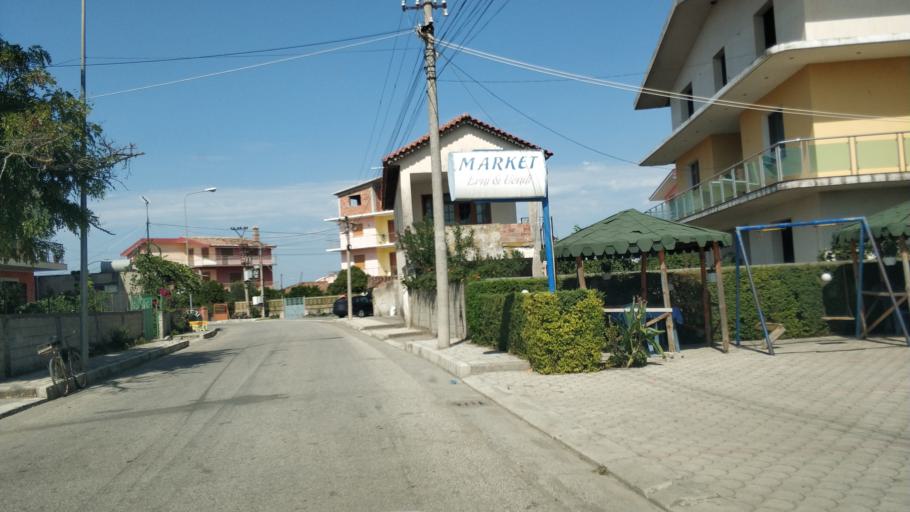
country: AL
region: Fier
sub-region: Rrethi i Lushnjes
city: Divjake
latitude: 40.9985
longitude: 19.5271
